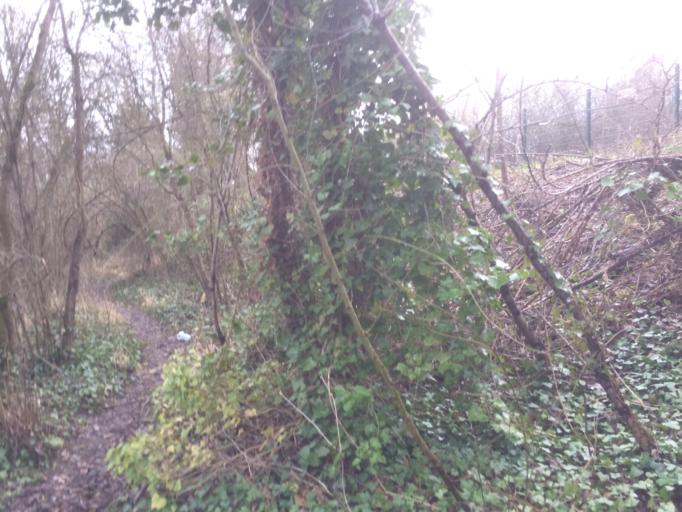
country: FR
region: Ile-de-France
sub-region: Departement de l'Essonne
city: Ris-Orangis
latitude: 48.6639
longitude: 2.4115
